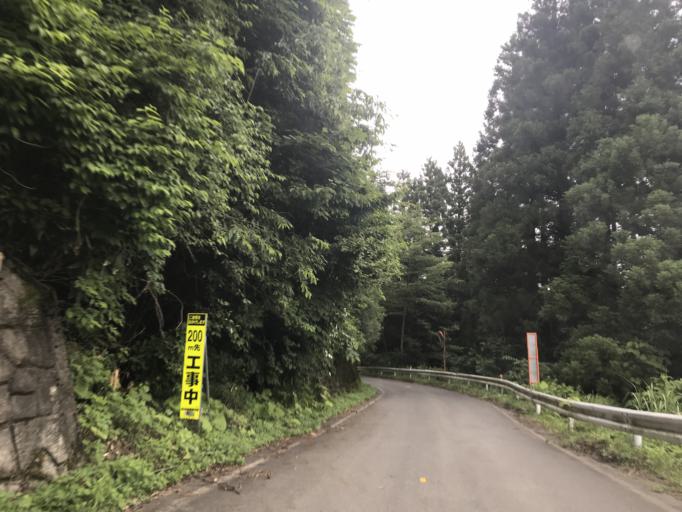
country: JP
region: Iwate
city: Ichinoseki
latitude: 38.9602
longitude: 140.8972
